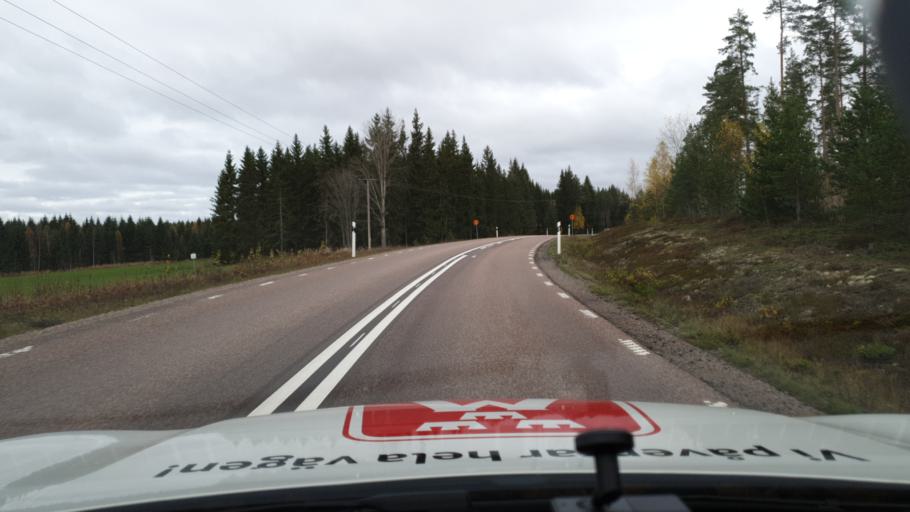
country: SE
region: Gaevleborg
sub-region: Gavle Kommun
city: Hedesunda
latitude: 60.4873
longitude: 16.9354
